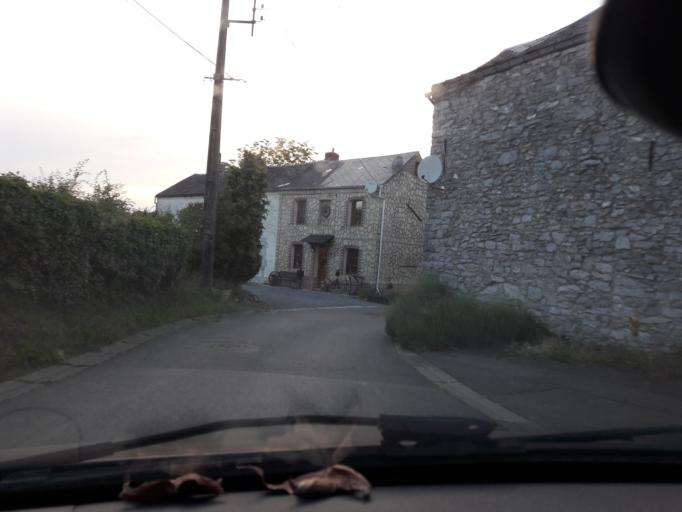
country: BE
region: Wallonia
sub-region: Province du Hainaut
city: Beaumont
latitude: 50.2606
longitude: 4.1809
